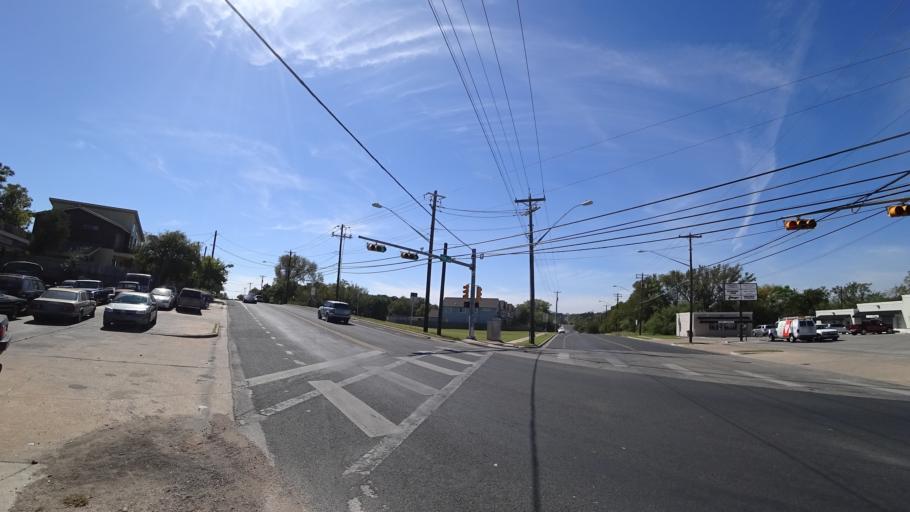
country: US
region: Texas
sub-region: Travis County
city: Austin
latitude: 30.2789
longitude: -97.6870
